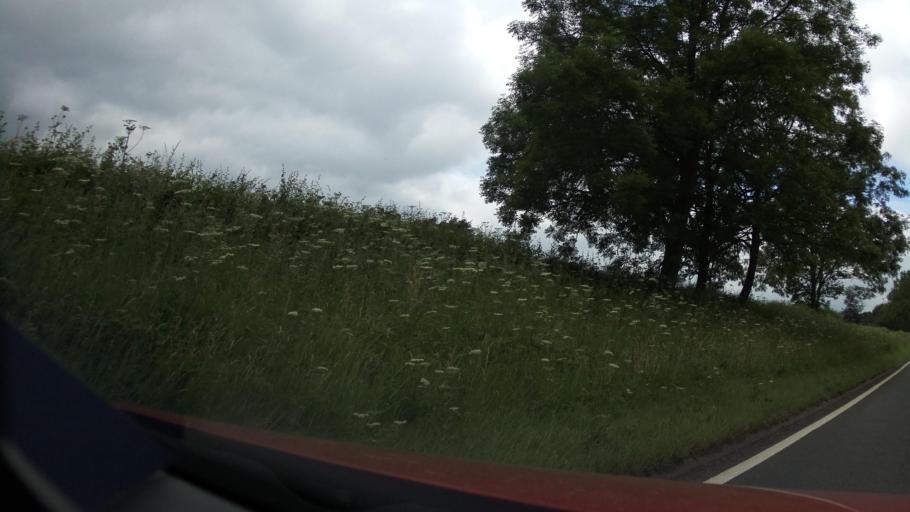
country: GB
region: England
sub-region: Derbyshire
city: Yeldersley
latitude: 52.9762
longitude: -1.6504
